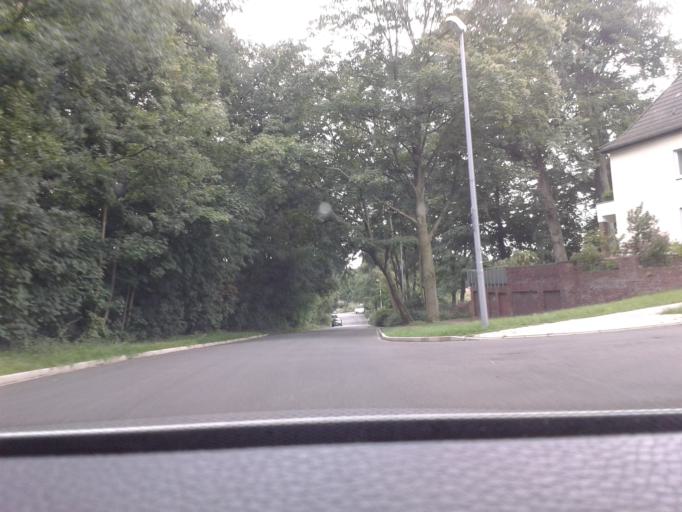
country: DE
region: North Rhine-Westphalia
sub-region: Regierungsbezirk Dusseldorf
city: Muelheim (Ruhr)
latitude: 51.4355
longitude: 6.8261
